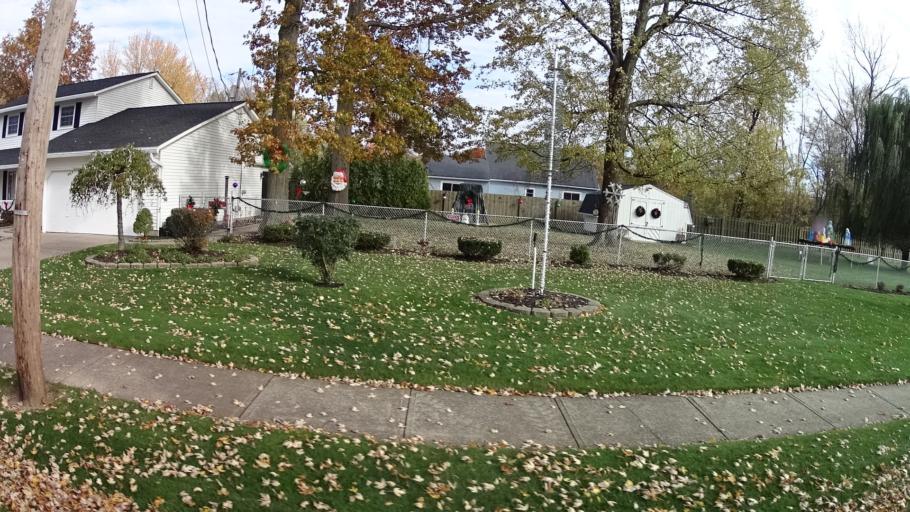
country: US
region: Ohio
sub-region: Lorain County
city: Sheffield Lake
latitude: 41.4887
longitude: -82.0965
